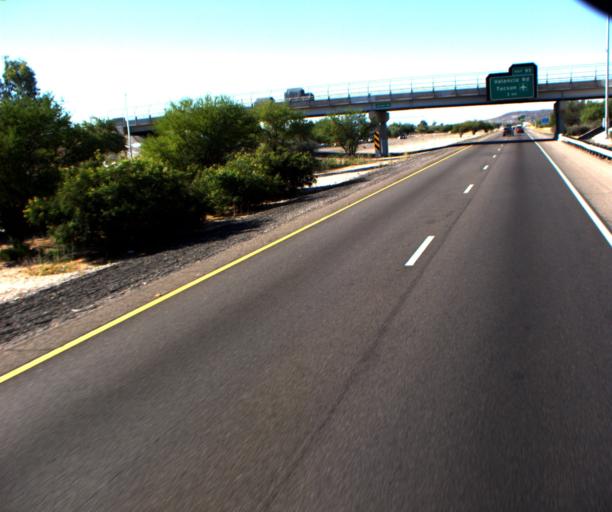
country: US
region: Arizona
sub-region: Pima County
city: Drexel Heights
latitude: 32.1493
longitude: -110.9869
